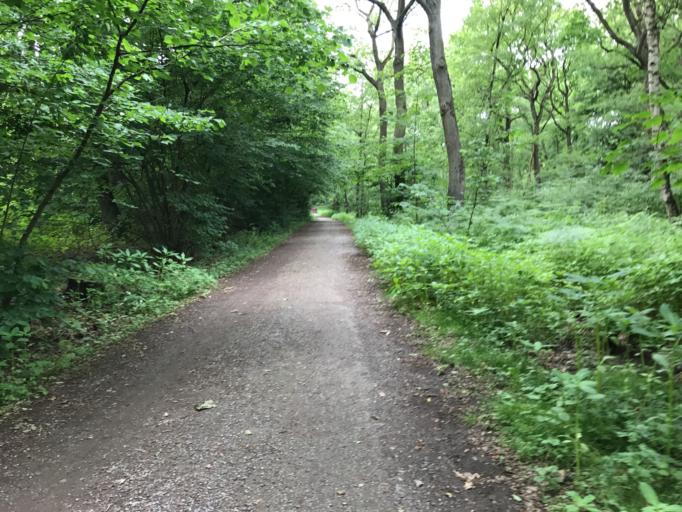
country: DE
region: North Rhine-Westphalia
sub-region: Regierungsbezirk Dusseldorf
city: Duisburg
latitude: 51.4164
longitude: 6.8128
